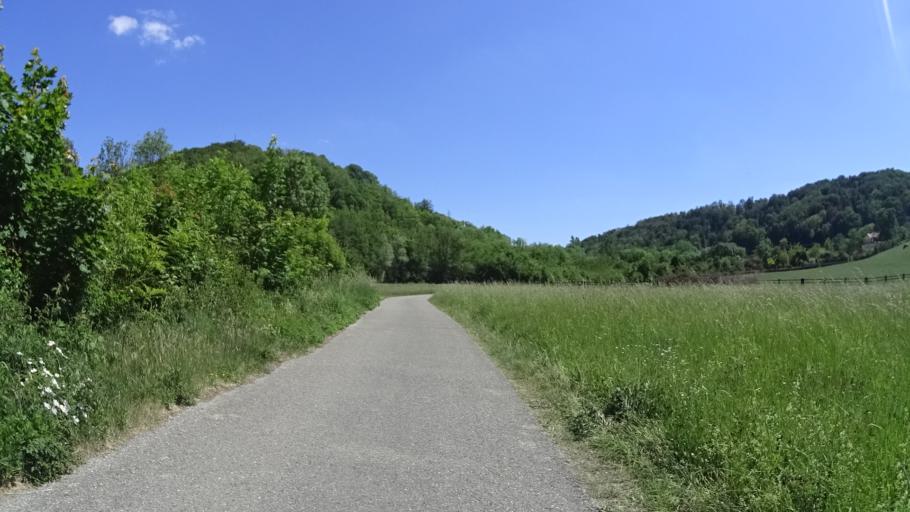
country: DE
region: Bavaria
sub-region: Regierungsbezirk Mittelfranken
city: Adelshofen
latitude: 49.4024
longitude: 10.1554
